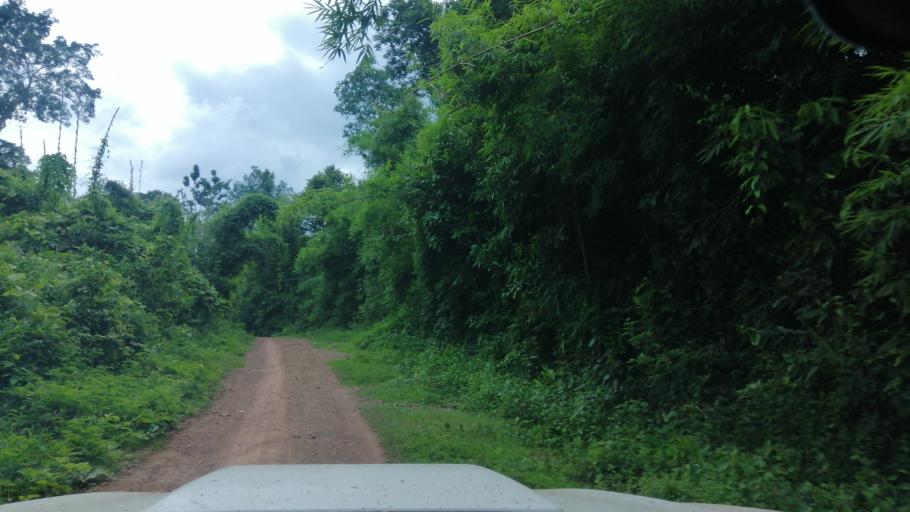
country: TH
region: Nan
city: Mae Charim
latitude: 18.7691
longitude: 101.3117
